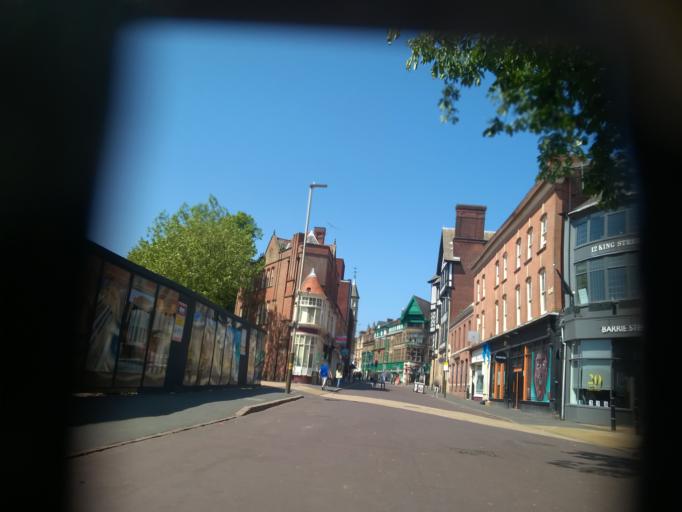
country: GB
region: England
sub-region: City of Leicester
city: Leicester
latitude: 52.6312
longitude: -1.1323
